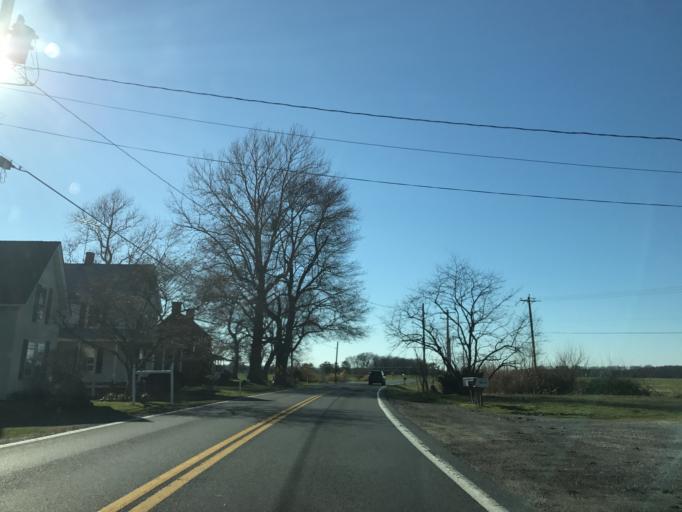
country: US
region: Maryland
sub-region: Caroline County
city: Ridgely
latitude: 39.0032
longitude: -75.9587
